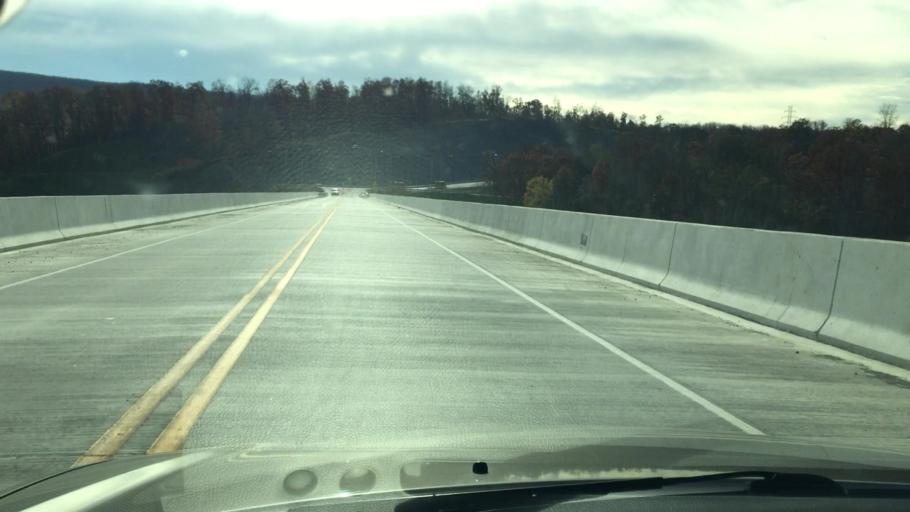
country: US
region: Pennsylvania
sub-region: Luzerne County
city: Nanticoke
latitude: 41.1999
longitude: -75.9642
